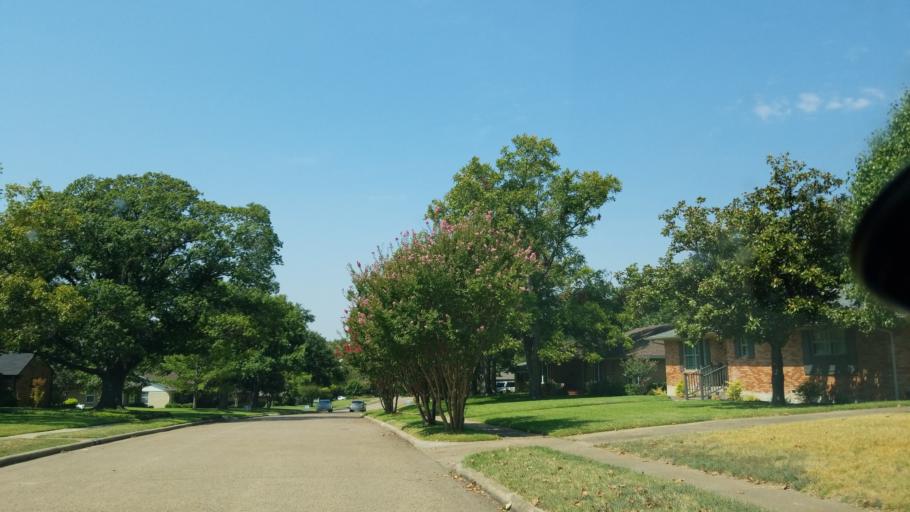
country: US
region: Texas
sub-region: Dallas County
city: Richardson
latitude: 32.8740
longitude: -96.7151
